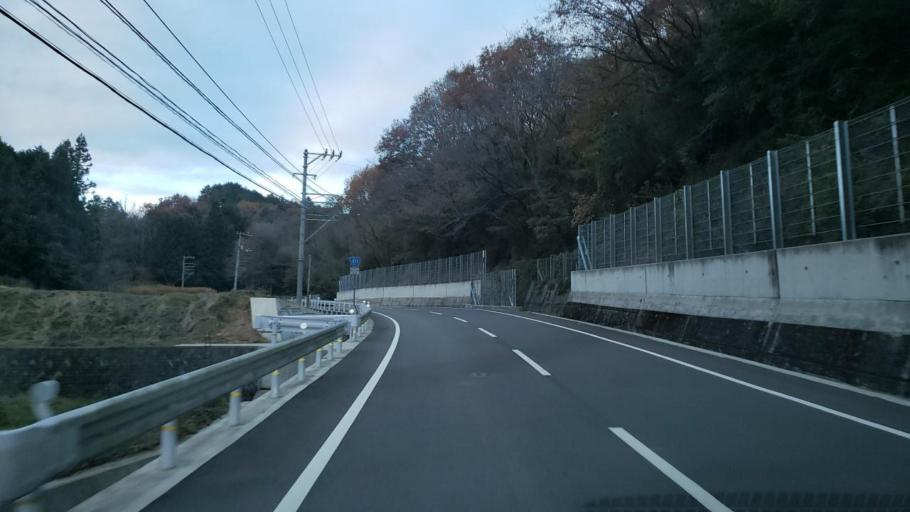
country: JP
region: Kagawa
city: Shido
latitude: 34.1960
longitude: 134.2507
